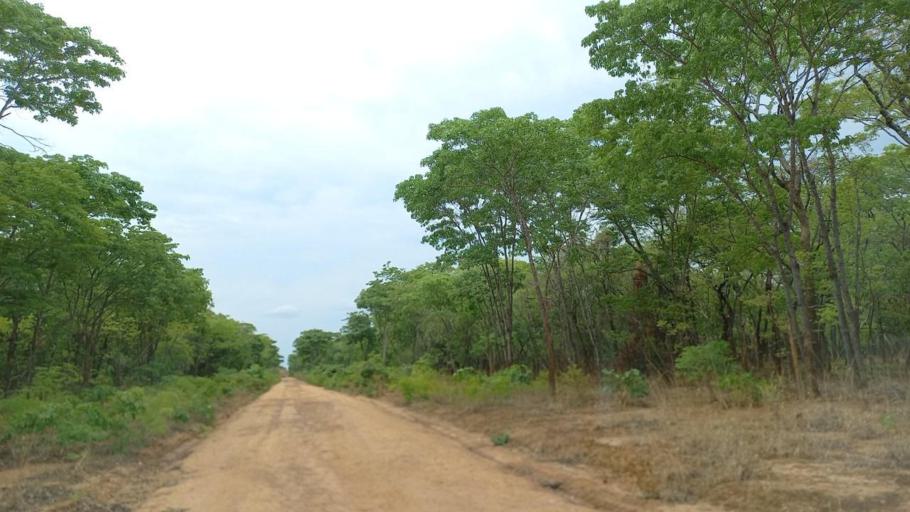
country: ZM
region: North-Western
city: Kalengwa
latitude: -13.5909
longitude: 24.9726
